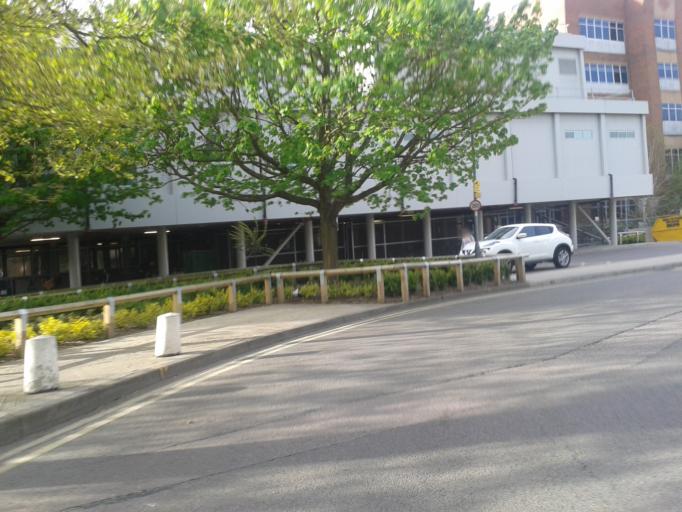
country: GB
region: England
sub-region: Cambridgeshire
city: Cambridge
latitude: 52.1752
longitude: 0.1393
